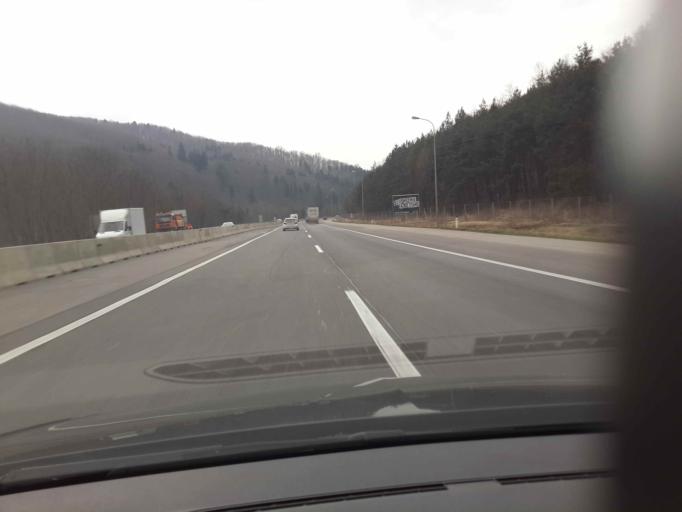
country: AT
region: Lower Austria
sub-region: Politischer Bezirk Baden
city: Alland
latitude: 48.0738
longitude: 16.0577
